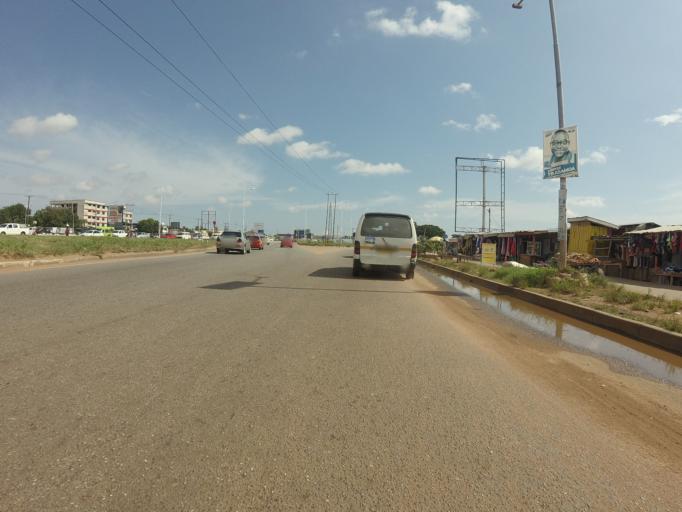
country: GH
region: Greater Accra
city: Medina Estates
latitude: 5.7082
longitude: -0.1714
